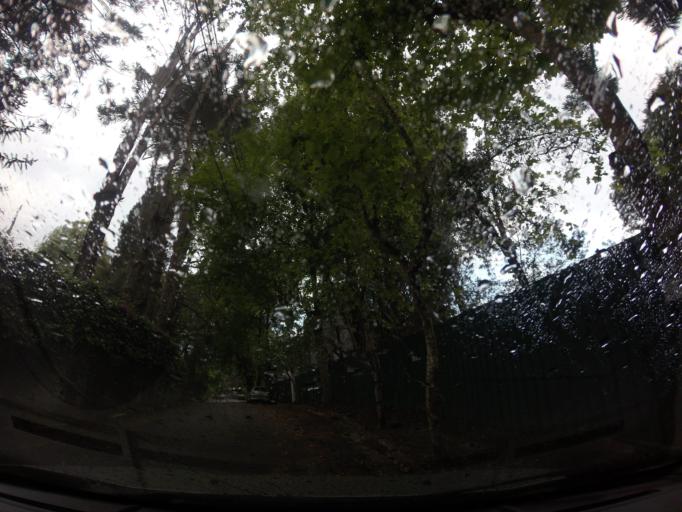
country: BR
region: Sao Paulo
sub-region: Campos Do Jordao
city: Campos do Jordao
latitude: -22.7224
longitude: -45.5678
